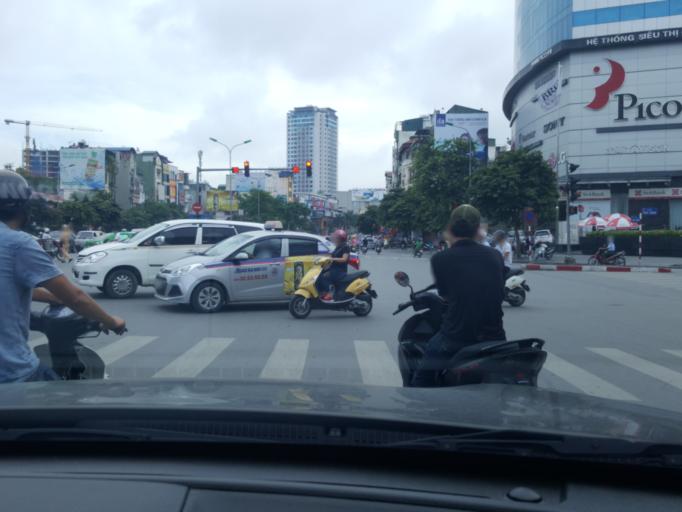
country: VN
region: Ha Noi
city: Dong Da
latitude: 21.0060
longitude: 105.8226
